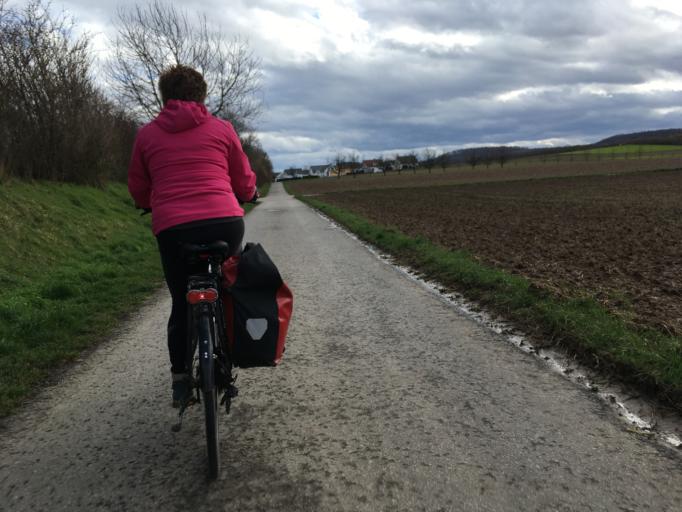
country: DE
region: Baden-Wuerttemberg
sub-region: Regierungsbezirk Stuttgart
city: Ellhofen
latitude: 49.1466
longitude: 9.3140
